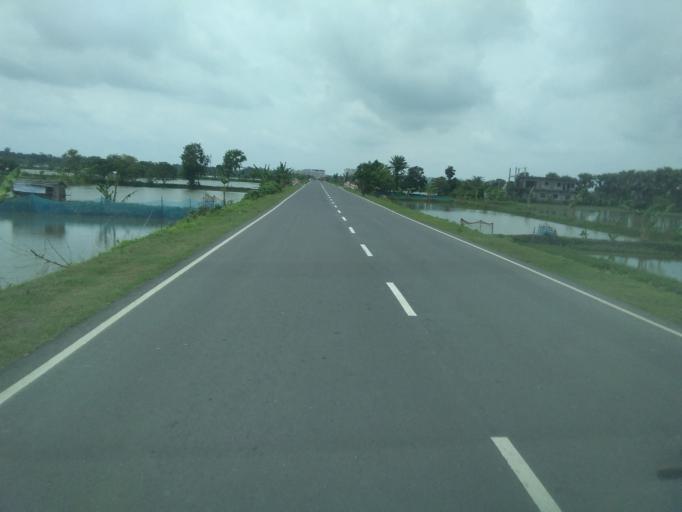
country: BD
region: Khulna
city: Satkhira
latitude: 22.7014
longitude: 89.0541
